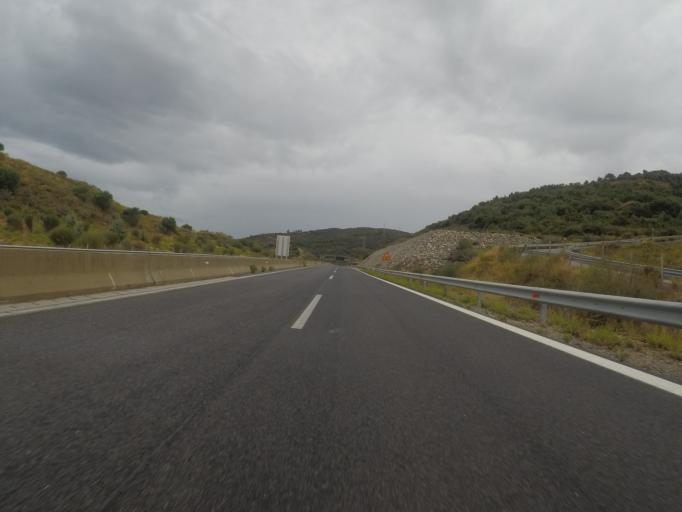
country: GR
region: Peloponnese
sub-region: Nomos Messinias
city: Meligalas
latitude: 37.2610
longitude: 22.0255
